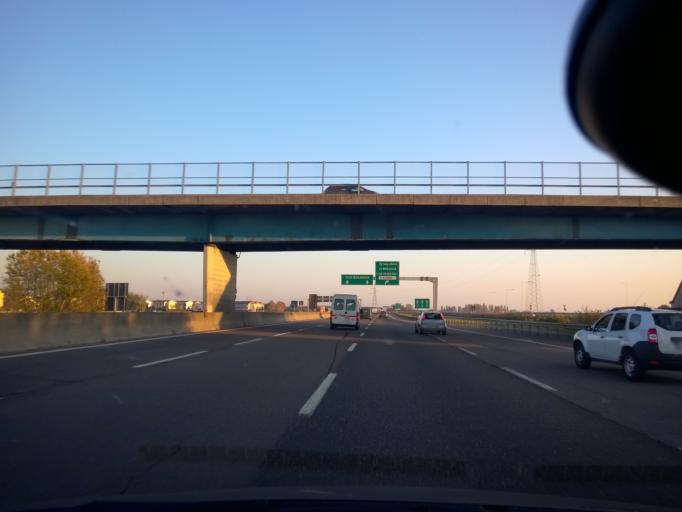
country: IT
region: Lombardy
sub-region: Citta metropolitana di Milano
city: Riozzo
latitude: 45.3467
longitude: 9.3128
